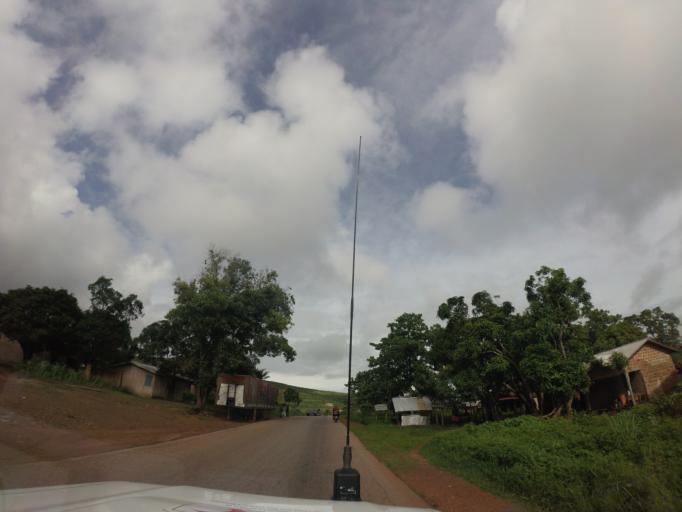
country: GN
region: Kindia
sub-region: Coyah
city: Coyah
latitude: 9.8293
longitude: -13.2448
